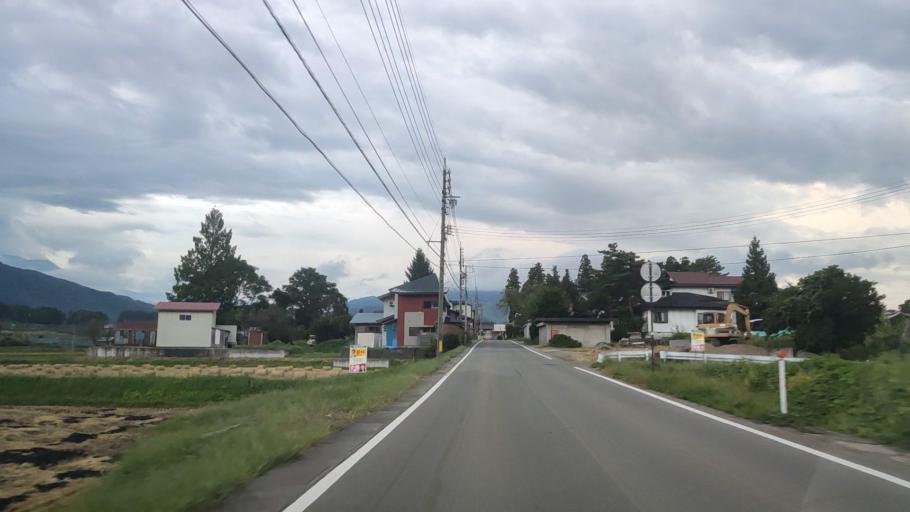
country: JP
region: Nagano
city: Iiyama
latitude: 36.8698
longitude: 138.4076
